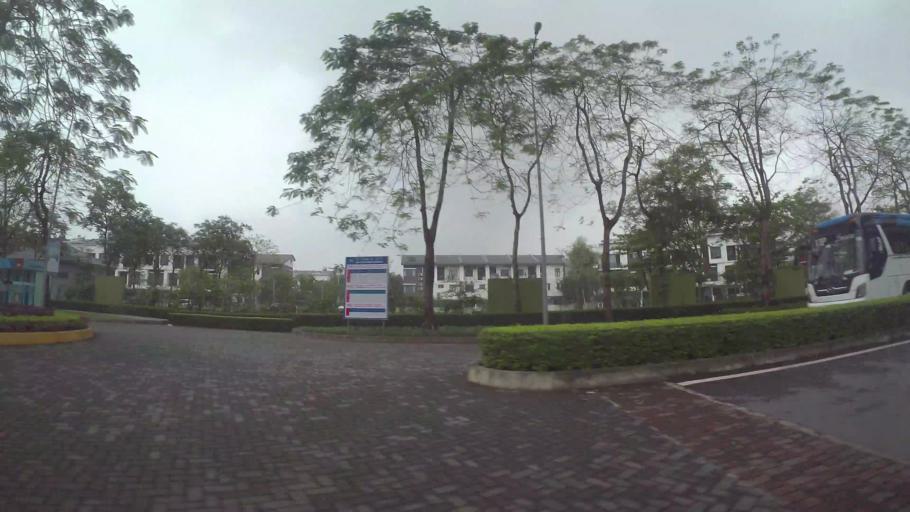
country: VN
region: Ha Noi
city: Van Dien
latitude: 20.9728
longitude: 105.8767
